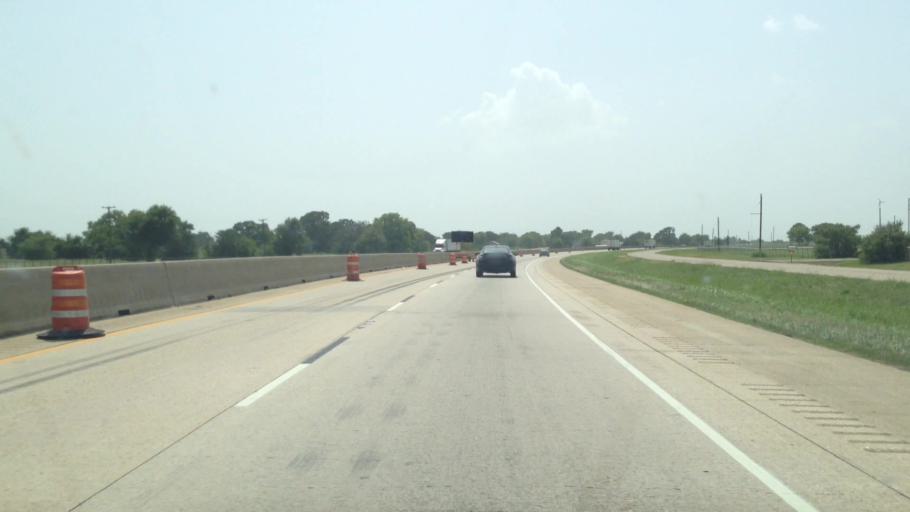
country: US
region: Texas
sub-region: Hopkins County
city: Sulphur Springs
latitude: 33.1196
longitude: -95.7175
